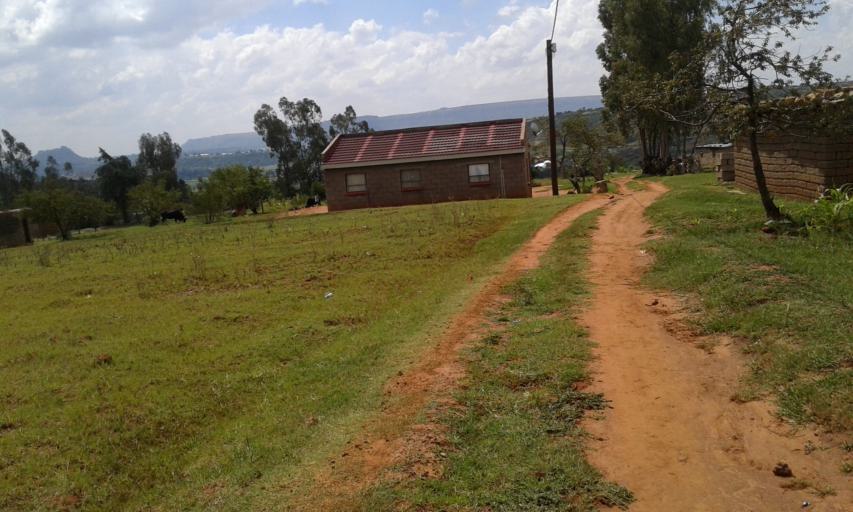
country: LS
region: Maseru
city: Maseru
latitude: -29.4230
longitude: 27.5718
